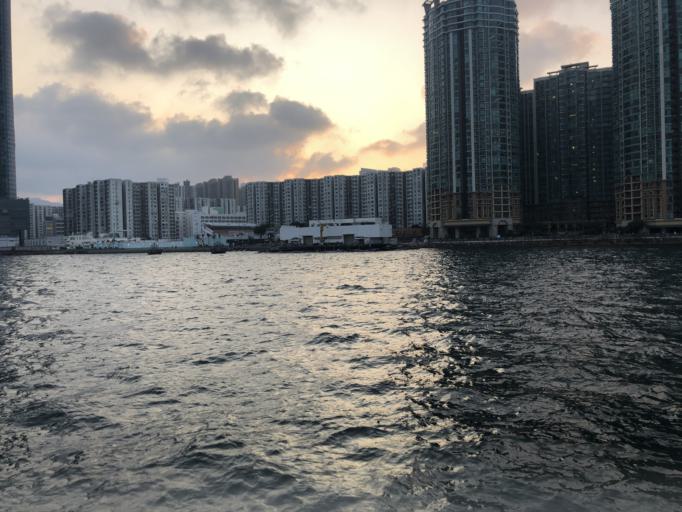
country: HK
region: Kowloon City
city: Kowloon
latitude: 22.3067
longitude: 114.1957
